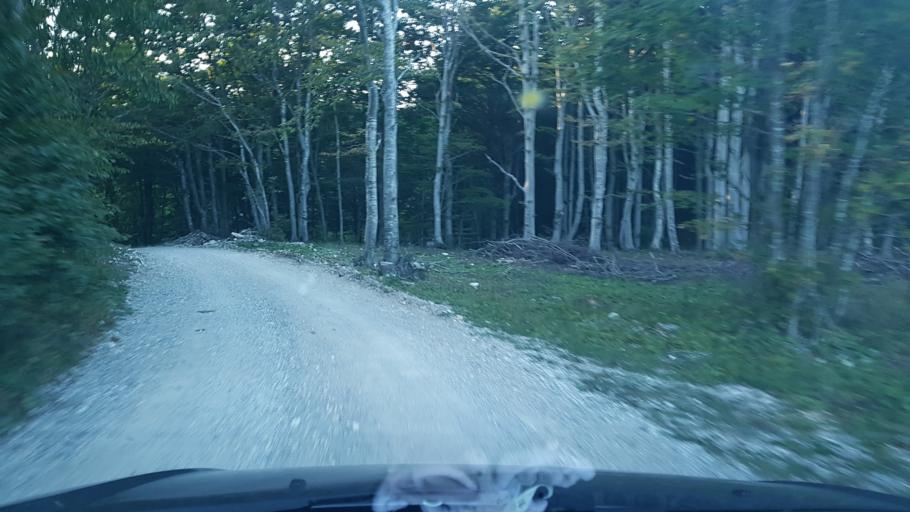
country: SI
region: Vipava
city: Vipava
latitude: 45.7733
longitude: 14.0501
